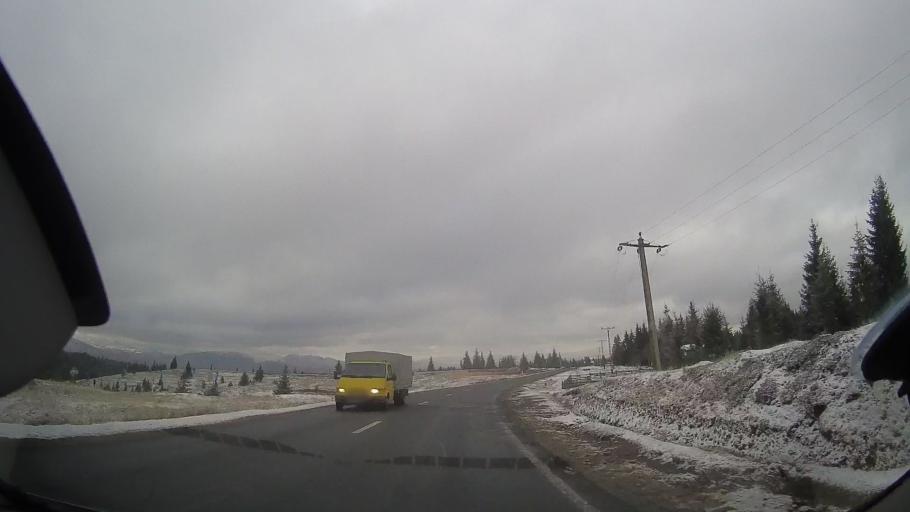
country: RO
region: Cluj
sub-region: Comuna Belis
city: Belis
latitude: 46.6981
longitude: 23.0367
